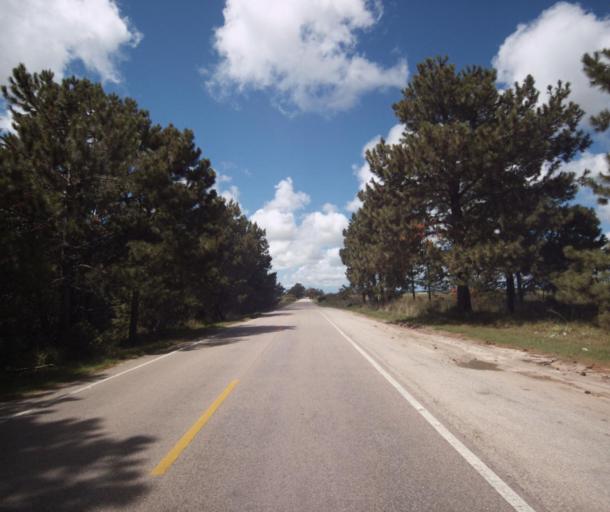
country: BR
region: Rio Grande do Sul
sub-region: Arroio Grande
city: Arroio Grande
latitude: -32.5282
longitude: -52.5443
